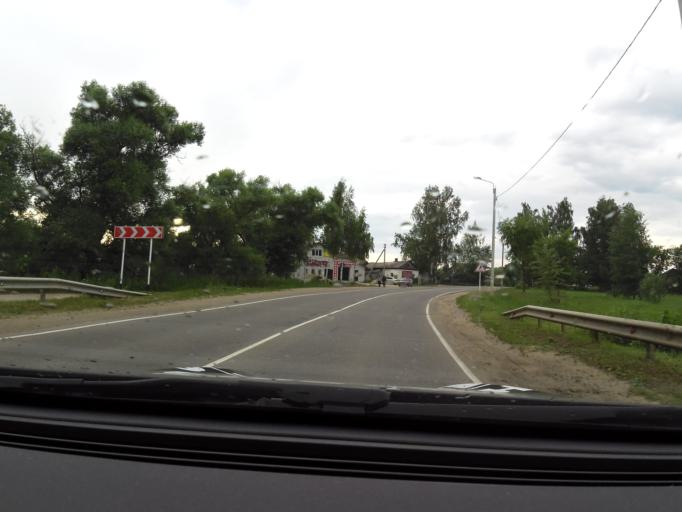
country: RU
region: Vladimir
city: Vorsha
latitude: 56.1030
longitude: 40.0770
